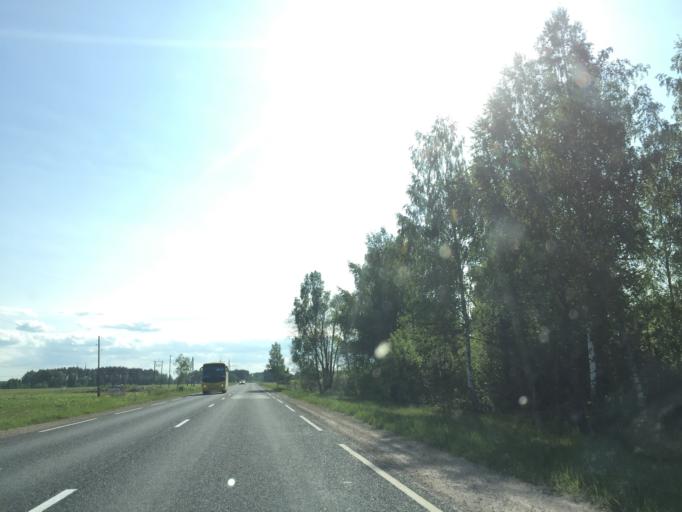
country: LV
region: Salaspils
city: Salaspils
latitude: 56.8228
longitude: 24.3069
